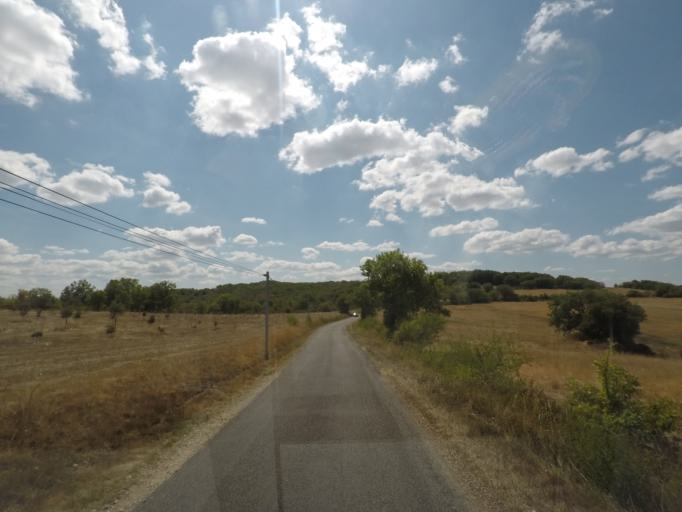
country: FR
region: Midi-Pyrenees
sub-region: Departement du Lot
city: Cajarc
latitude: 44.5395
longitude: 1.6695
